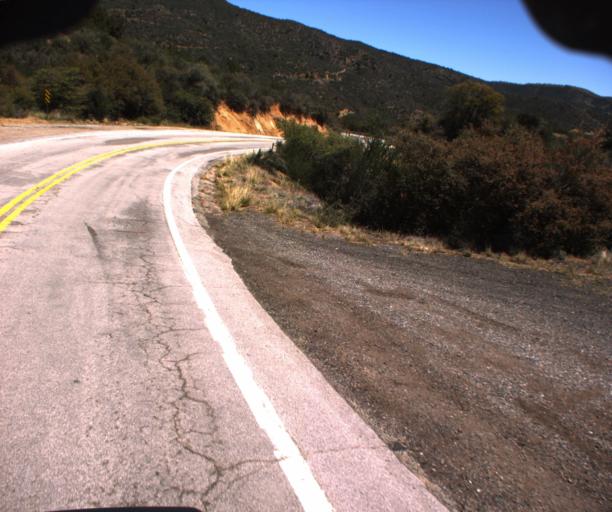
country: US
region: Arizona
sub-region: Yavapai County
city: Prescott
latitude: 34.4497
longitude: -112.5391
